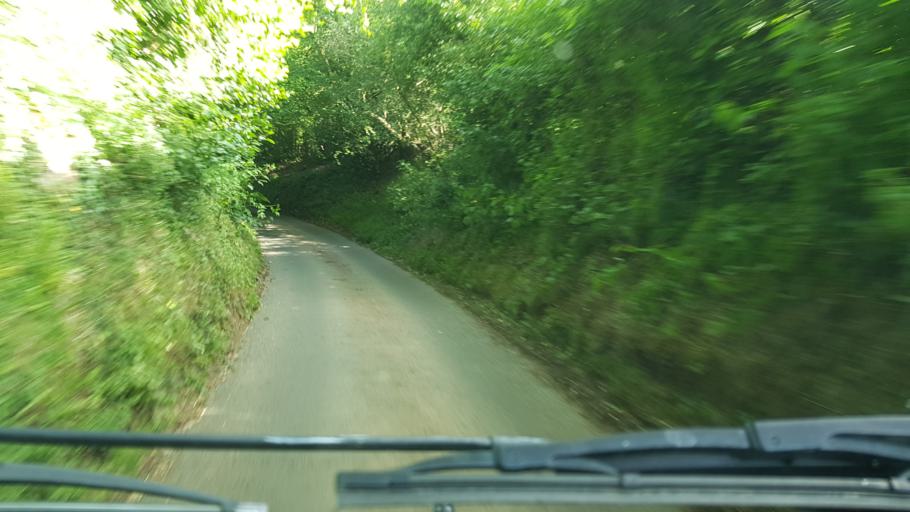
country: GB
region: England
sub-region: Worcestershire
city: Bewdley
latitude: 52.3475
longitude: -2.3309
